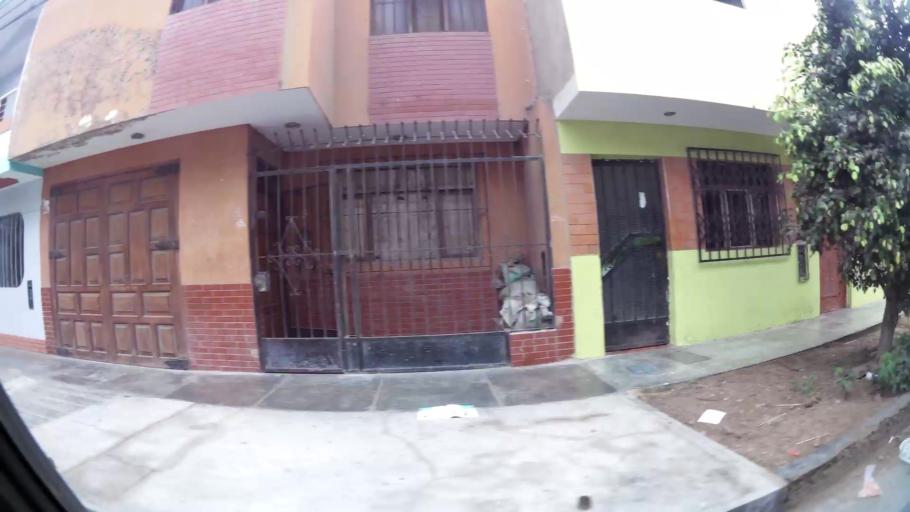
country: PE
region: La Libertad
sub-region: Provincia de Trujillo
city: La Esperanza
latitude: -8.0971
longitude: -79.0435
